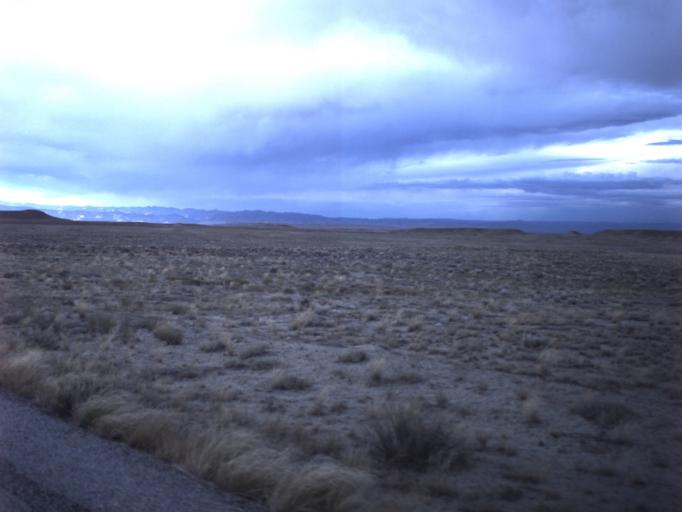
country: US
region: Utah
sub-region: Grand County
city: Moab
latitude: 38.9141
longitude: -109.3268
